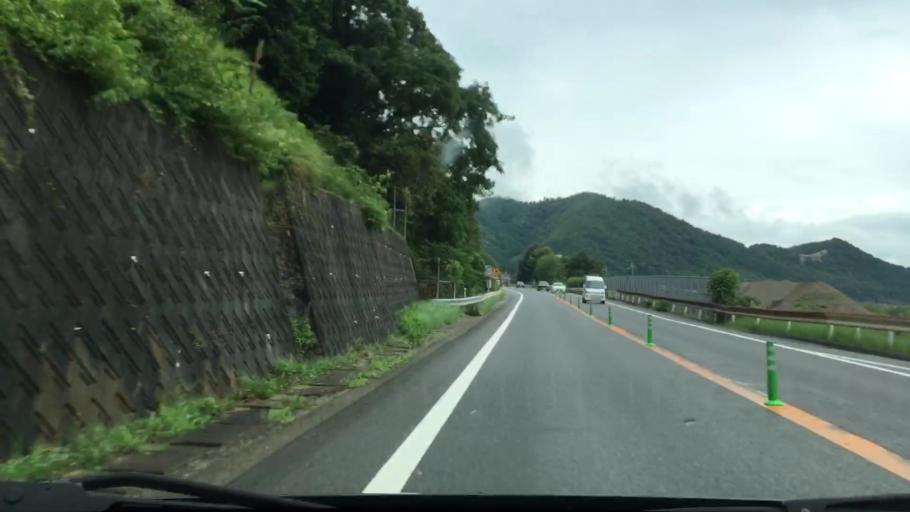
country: JP
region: Hyogo
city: Himeji
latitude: 35.0102
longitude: 134.7620
